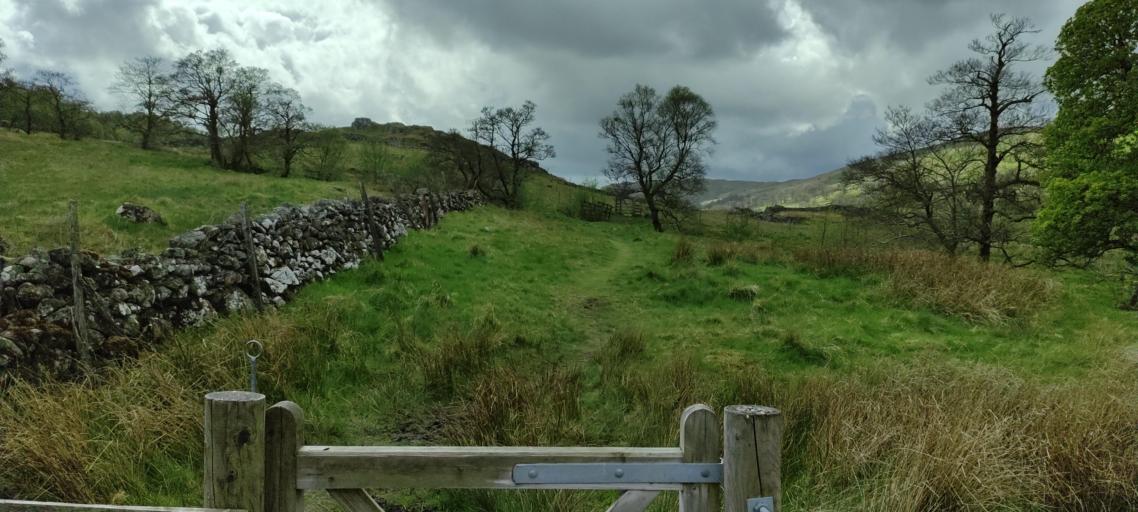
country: GB
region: England
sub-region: Cumbria
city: Kendal
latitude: 54.4935
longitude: -2.7025
